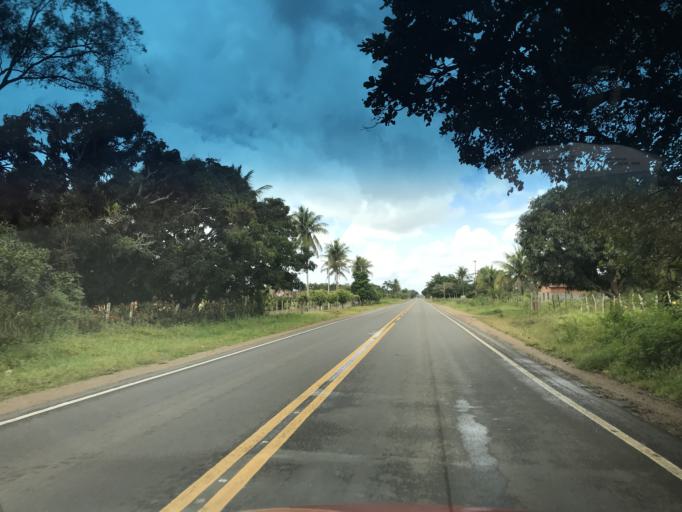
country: BR
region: Bahia
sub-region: Conceicao Do Almeida
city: Conceicao do Almeida
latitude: -12.7192
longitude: -39.2155
